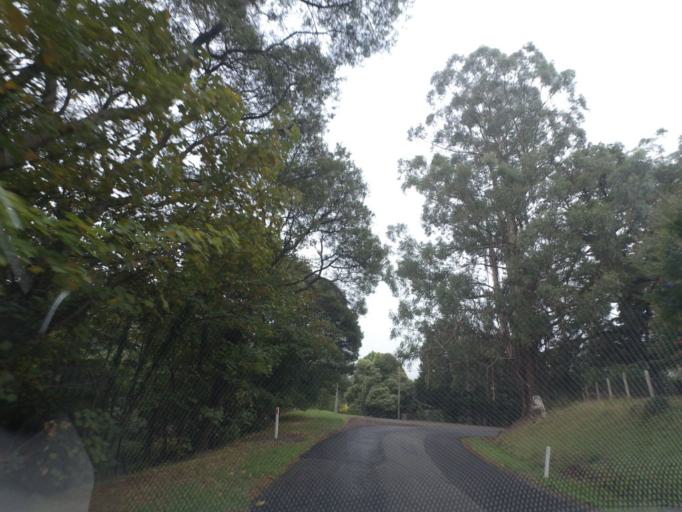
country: AU
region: Victoria
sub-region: Yarra Ranges
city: Yarra Junction
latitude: -37.7297
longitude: 145.5930
